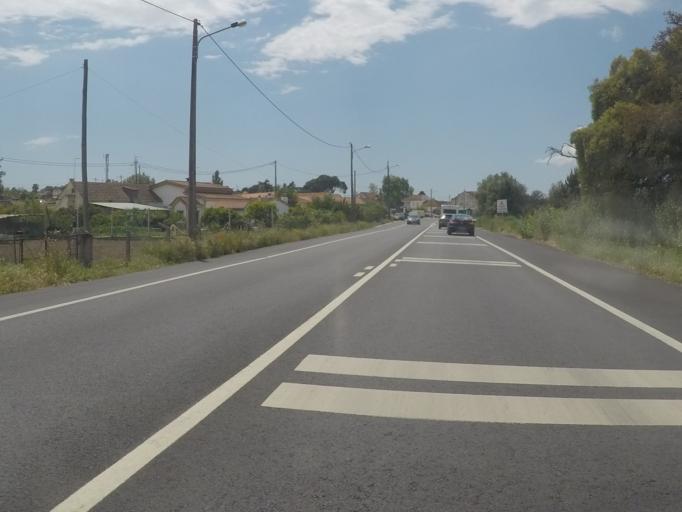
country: PT
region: Setubal
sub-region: Setubal
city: Setubal
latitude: 38.5474
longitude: -8.8149
